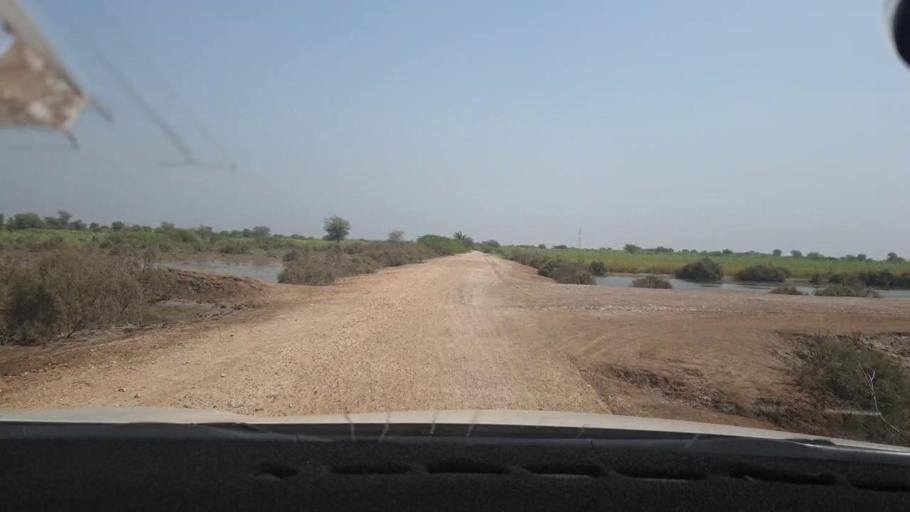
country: PK
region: Sindh
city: Tando Mittha Khan
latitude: 25.9231
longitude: 69.2335
